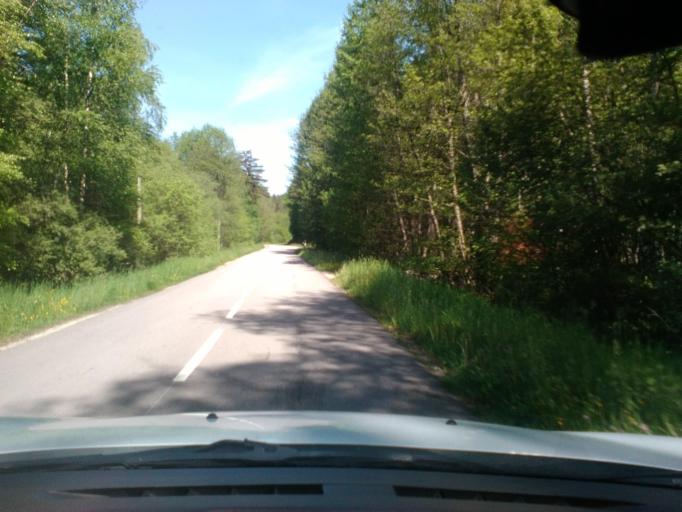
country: FR
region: Lorraine
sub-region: Departement des Vosges
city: Bruyeres
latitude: 48.2672
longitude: 6.7256
